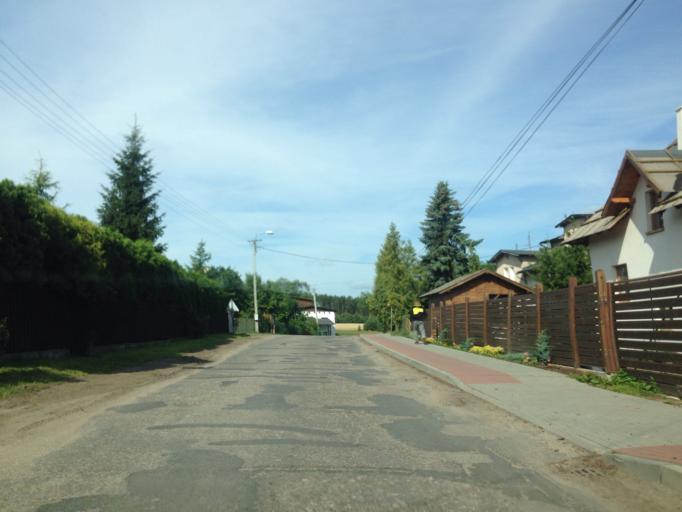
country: PL
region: Kujawsko-Pomorskie
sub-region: Powiat tucholski
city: Sliwice
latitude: 53.7234
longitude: 18.2102
